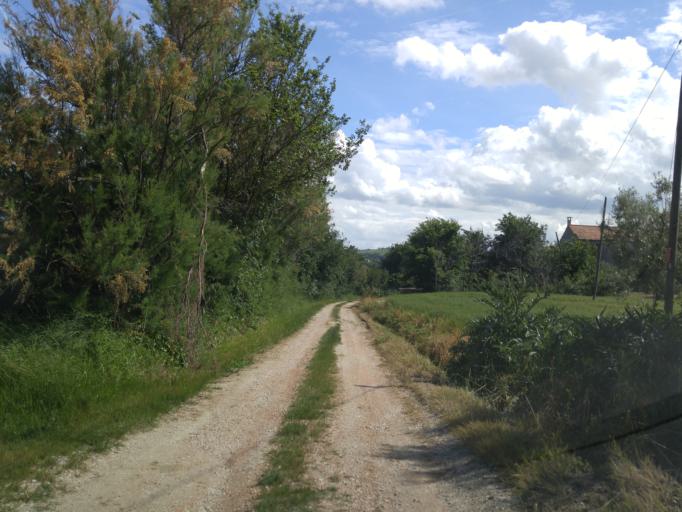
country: IT
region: The Marches
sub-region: Provincia di Pesaro e Urbino
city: San Costanzo
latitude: 43.7865
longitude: 13.0559
